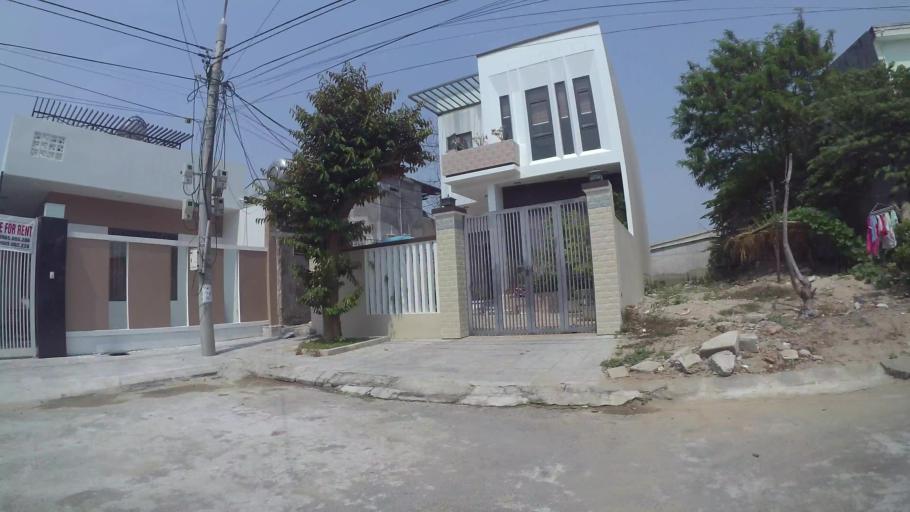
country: VN
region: Da Nang
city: Ngu Hanh Son
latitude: 16.0066
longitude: 108.2569
